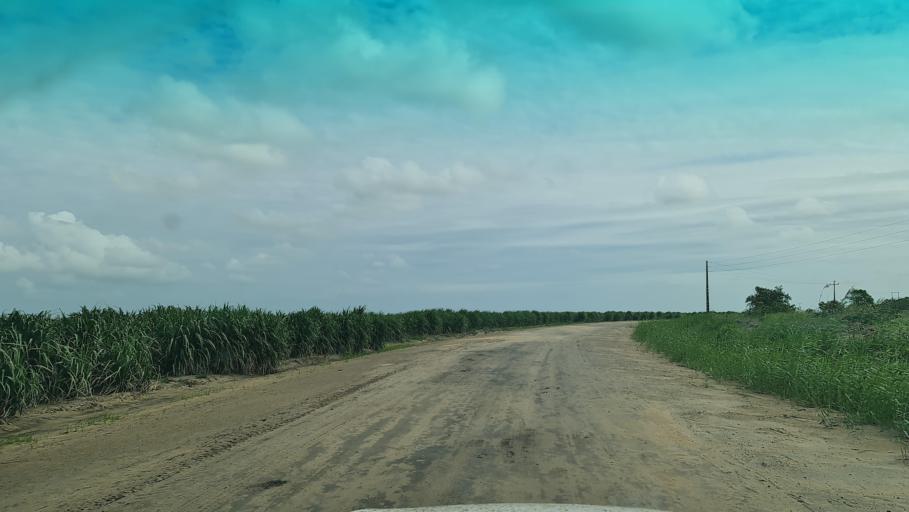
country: MZ
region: Maputo
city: Manhica
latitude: -25.4621
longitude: 32.8187
